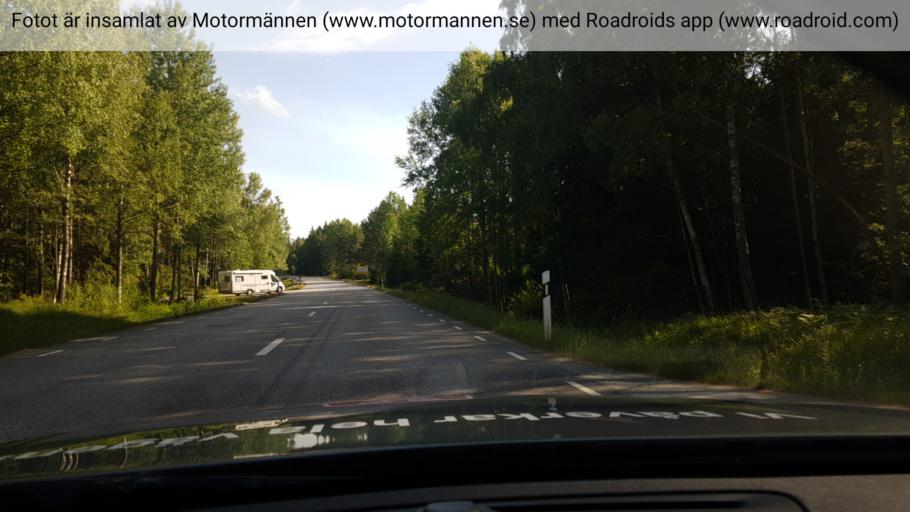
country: SE
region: Vaestra Goetaland
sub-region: Karlsborgs Kommun
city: Karlsborg
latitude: 58.6211
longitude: 14.5328
